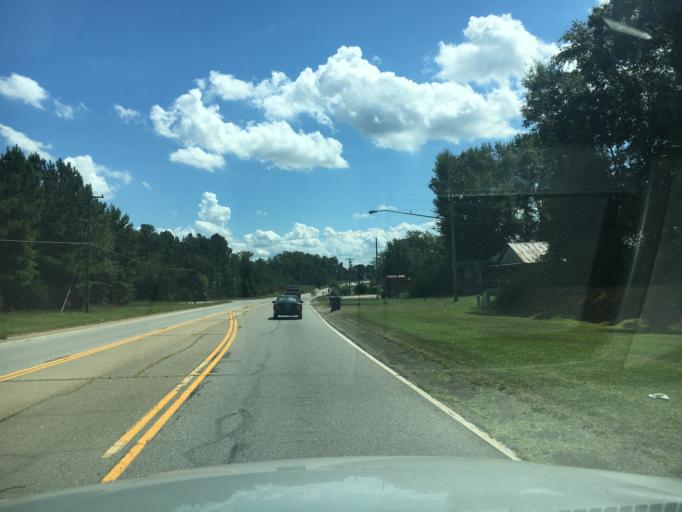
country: US
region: South Carolina
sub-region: Laurens County
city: Laurens
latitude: 34.5012
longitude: -82.0565
